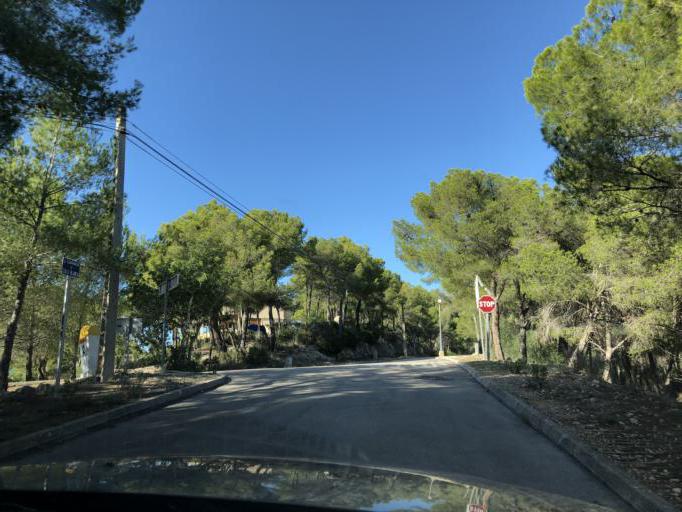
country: ES
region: Balearic Islands
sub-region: Illes Balears
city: Camp de Mar
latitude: 39.5395
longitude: 2.4054
